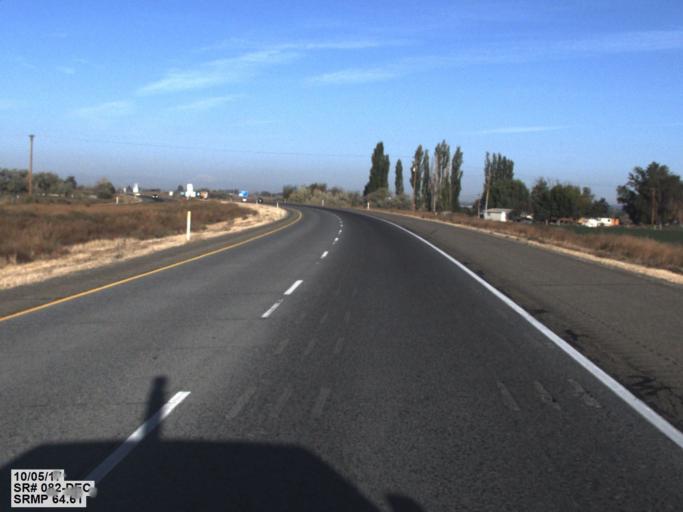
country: US
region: Washington
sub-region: Yakima County
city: Sunnyside
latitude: 46.3202
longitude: -120.0598
